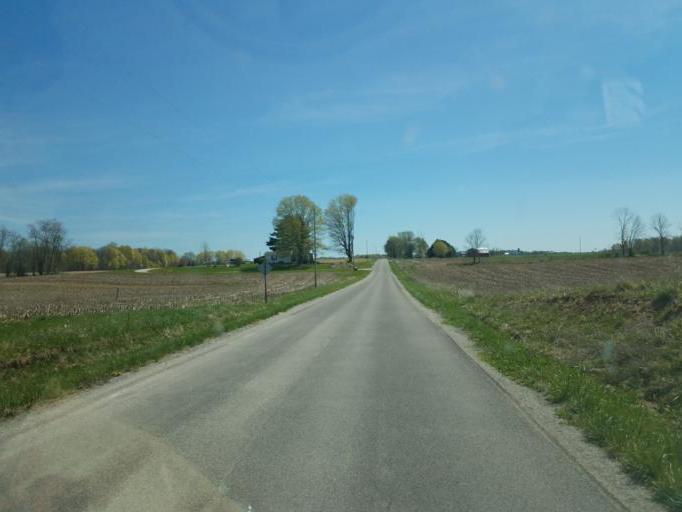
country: US
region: Ohio
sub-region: Morrow County
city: Mount Gilead
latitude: 40.5959
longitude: -82.7840
